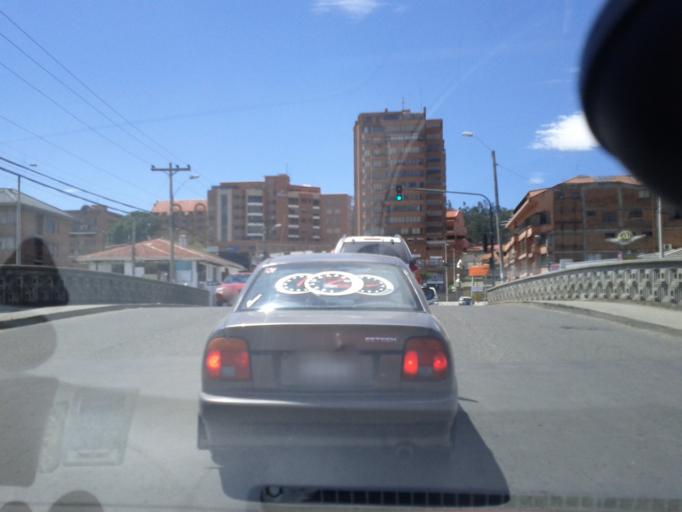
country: EC
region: Azuay
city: Cuenca
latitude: -2.8932
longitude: -79.0189
